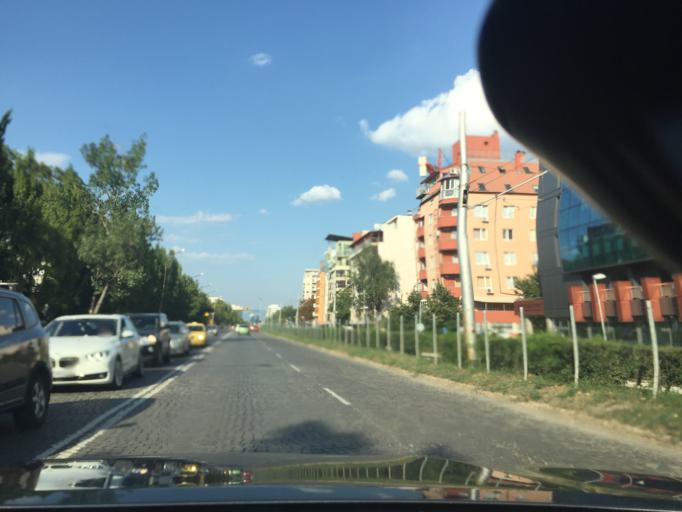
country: BG
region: Sofia-Capital
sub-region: Stolichna Obshtina
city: Sofia
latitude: 42.6801
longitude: 23.2875
